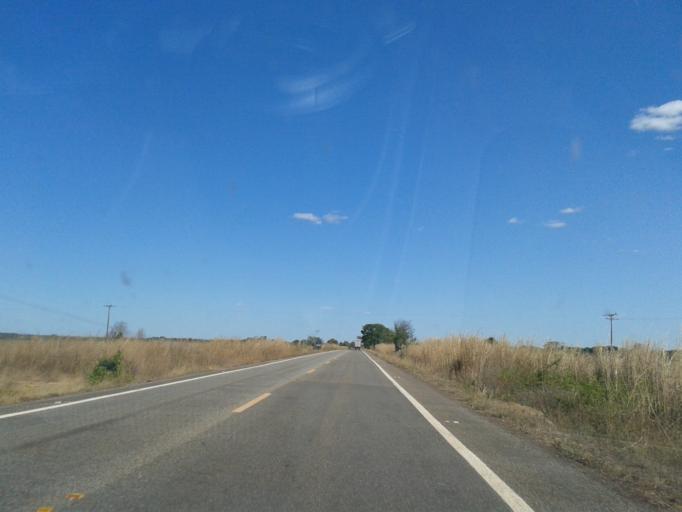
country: BR
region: Goias
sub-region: Sao Miguel Do Araguaia
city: Sao Miguel do Araguaia
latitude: -13.6017
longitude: -50.3196
